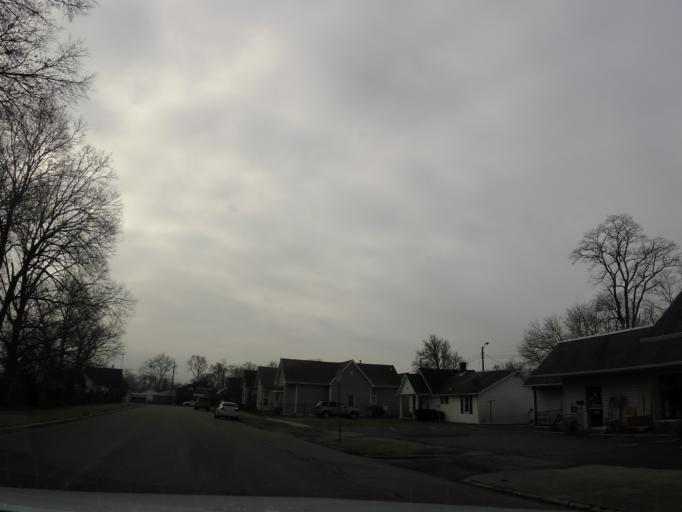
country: US
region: Indiana
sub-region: Bartholomew County
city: Columbus
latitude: 39.2158
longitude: -85.9121
